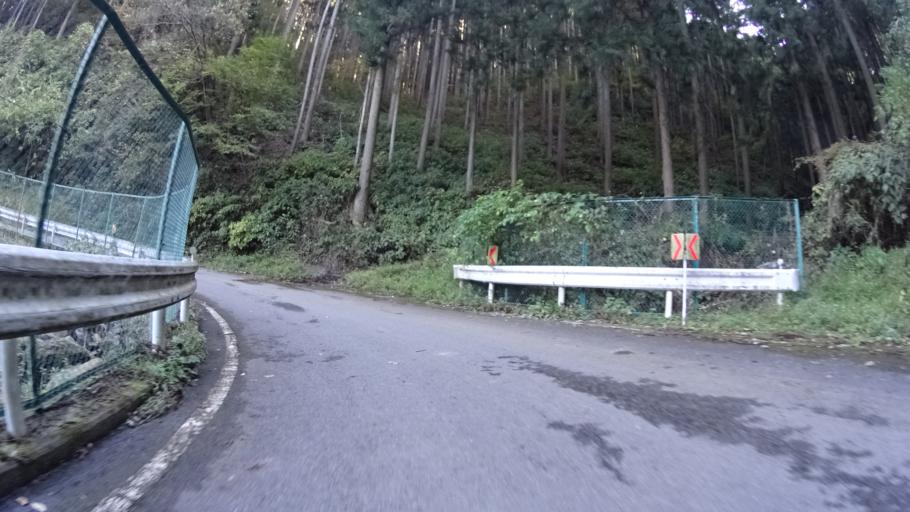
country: JP
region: Yamanashi
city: Uenohara
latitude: 35.6561
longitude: 139.1598
